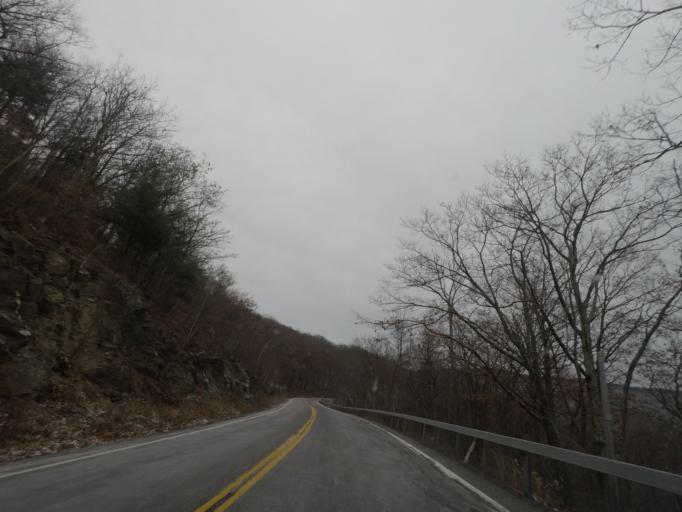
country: US
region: Massachusetts
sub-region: Berkshire County
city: Williamstown
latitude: 42.7407
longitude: -73.2827
